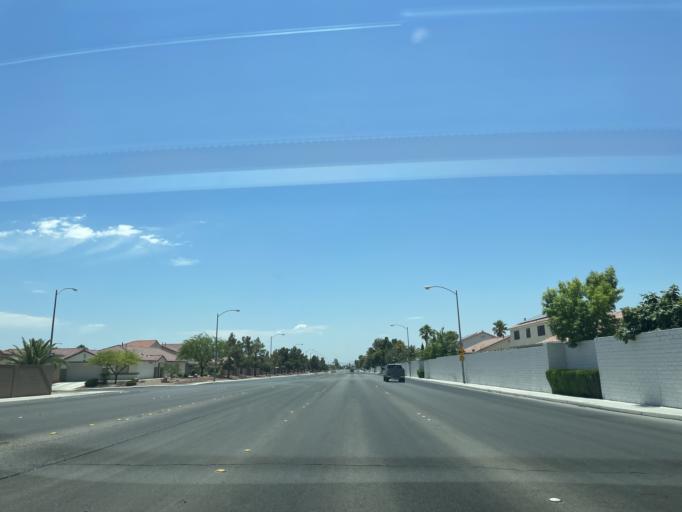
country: US
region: Nevada
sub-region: Clark County
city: North Las Vegas
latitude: 36.2734
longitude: -115.1532
